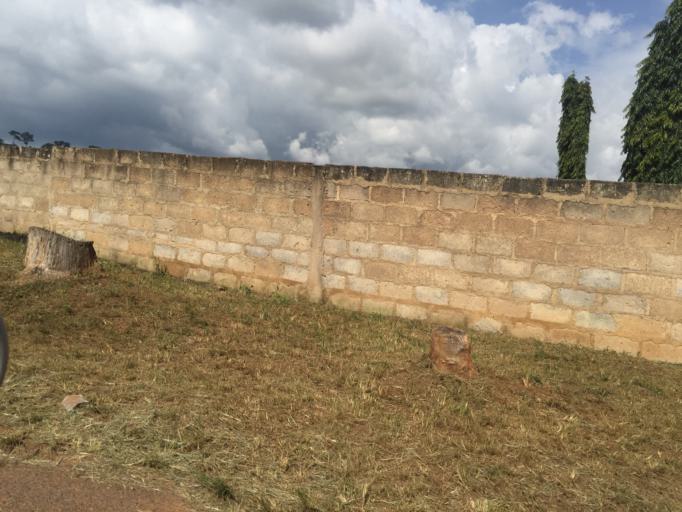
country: GH
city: Mpraeso
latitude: 6.6010
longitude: -0.7398
